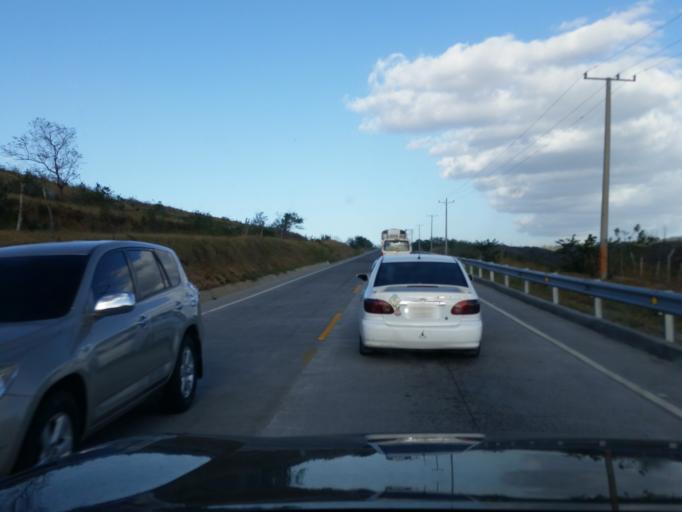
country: NI
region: Managua
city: Carlos Fonseca Amador
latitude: 12.0708
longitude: -86.4366
